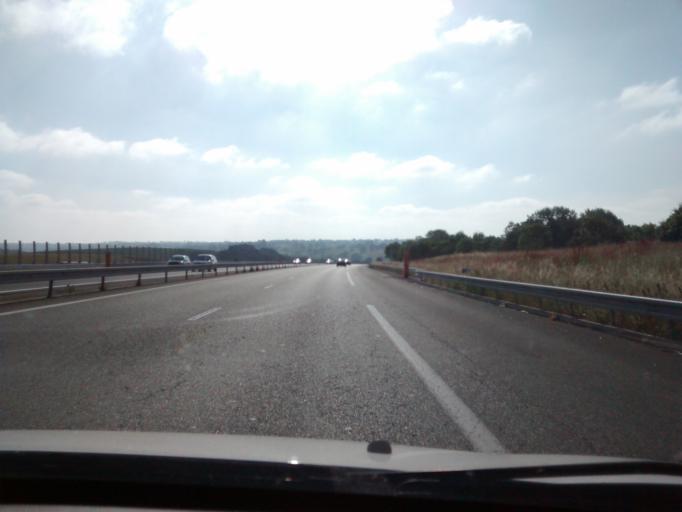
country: FR
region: Pays de la Loire
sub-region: Departement de la Mayenne
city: Change
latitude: 48.1160
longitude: -0.7859
